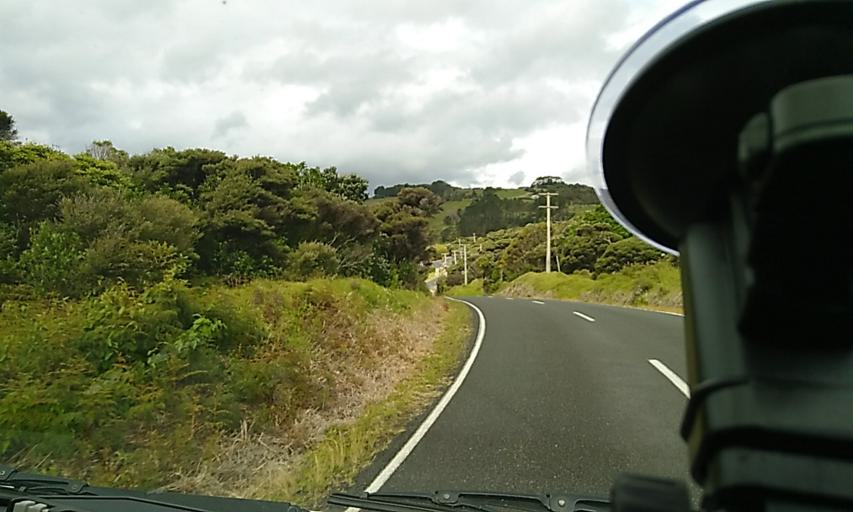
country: NZ
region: Northland
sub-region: Far North District
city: Ahipara
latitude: -35.5381
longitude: 173.3799
